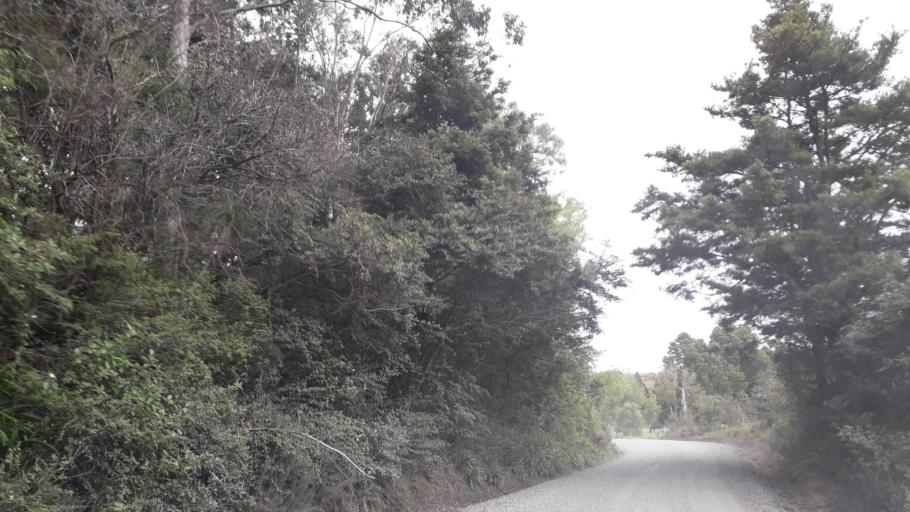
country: NZ
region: Northland
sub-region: Far North District
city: Kerikeri
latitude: -35.1191
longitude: 173.7517
